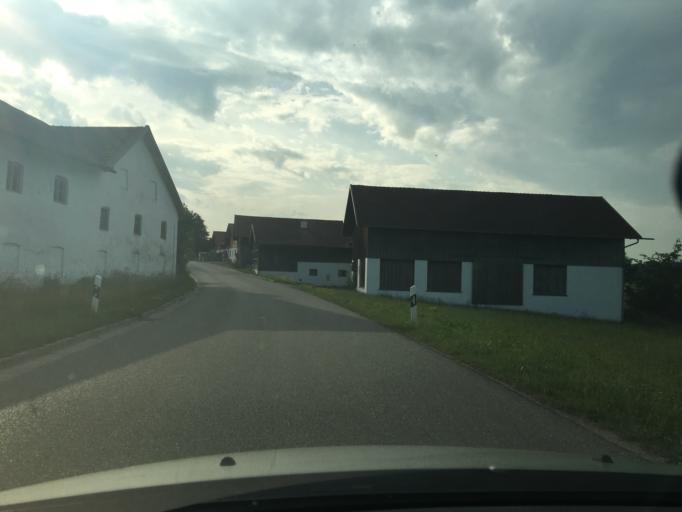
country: DE
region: Bavaria
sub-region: Upper Bavaria
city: Egglkofen
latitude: 48.3792
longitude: 12.4231
